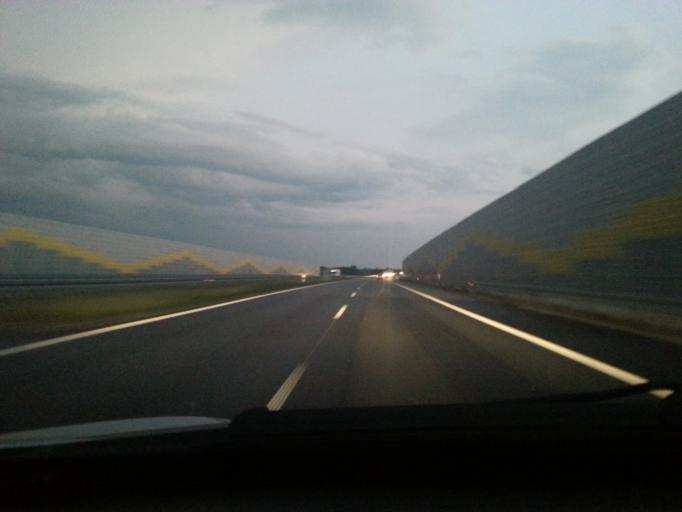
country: PL
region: Lodz Voivodeship
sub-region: Powiat sieradzki
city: Sieradz
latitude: 51.5745
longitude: 18.7905
